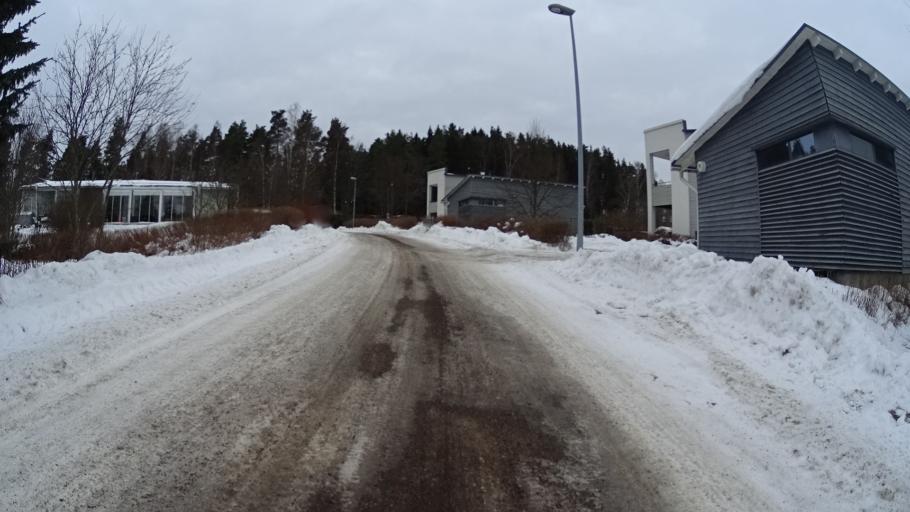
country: FI
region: Uusimaa
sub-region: Helsinki
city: Kauniainen
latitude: 60.2488
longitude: 24.7188
